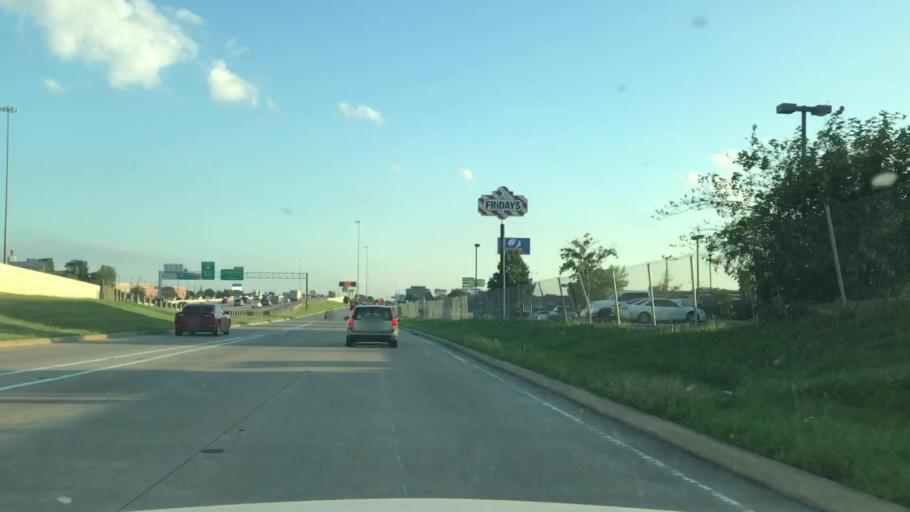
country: US
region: Texas
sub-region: Dallas County
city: Mesquite
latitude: 32.8156
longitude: -96.6290
